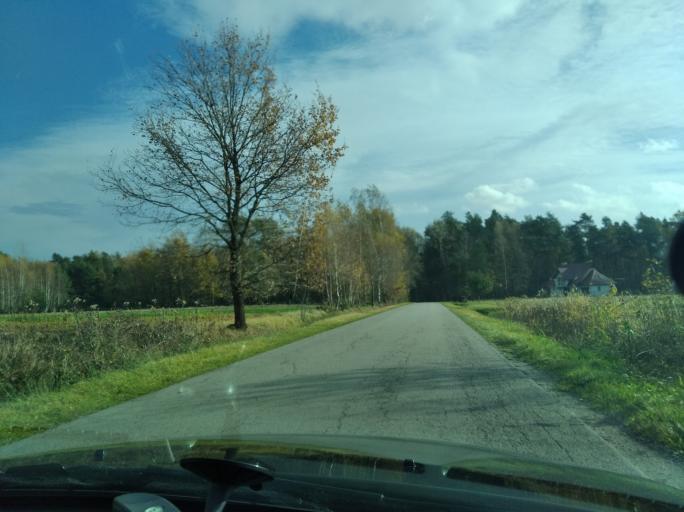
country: PL
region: Subcarpathian Voivodeship
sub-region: Powiat ropczycko-sedziszowski
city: Sedziszow Malopolski
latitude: 50.1221
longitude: 21.7129
